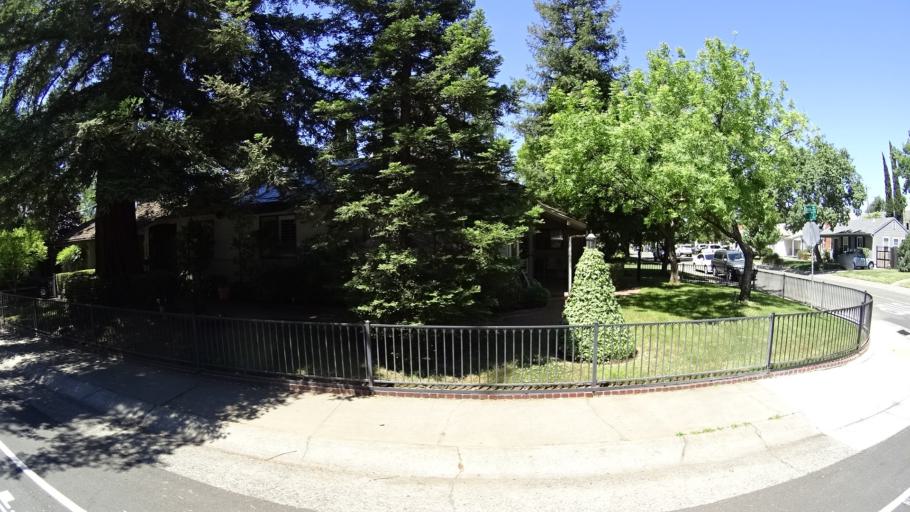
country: US
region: California
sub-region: Sacramento County
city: Sacramento
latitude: 38.5737
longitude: -121.4340
